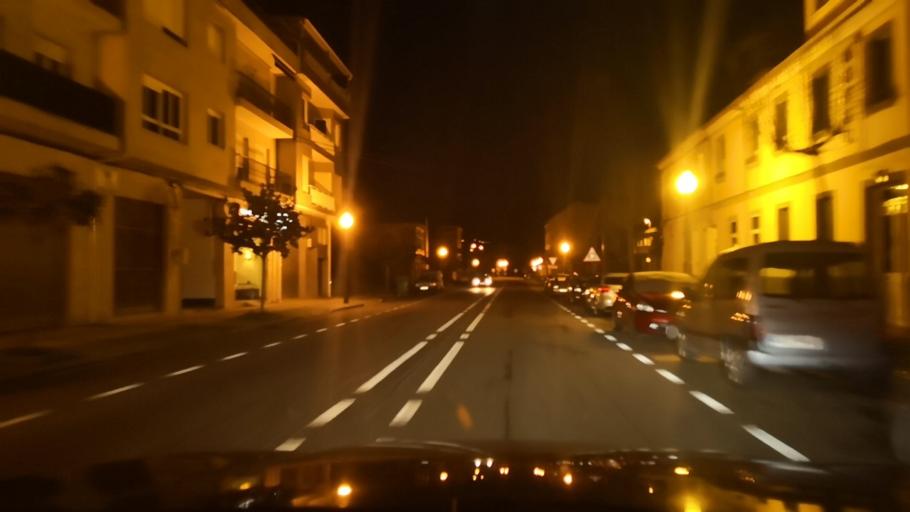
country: ES
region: Galicia
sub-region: Provincia de Ourense
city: Verin
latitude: 41.9399
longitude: -7.4253
